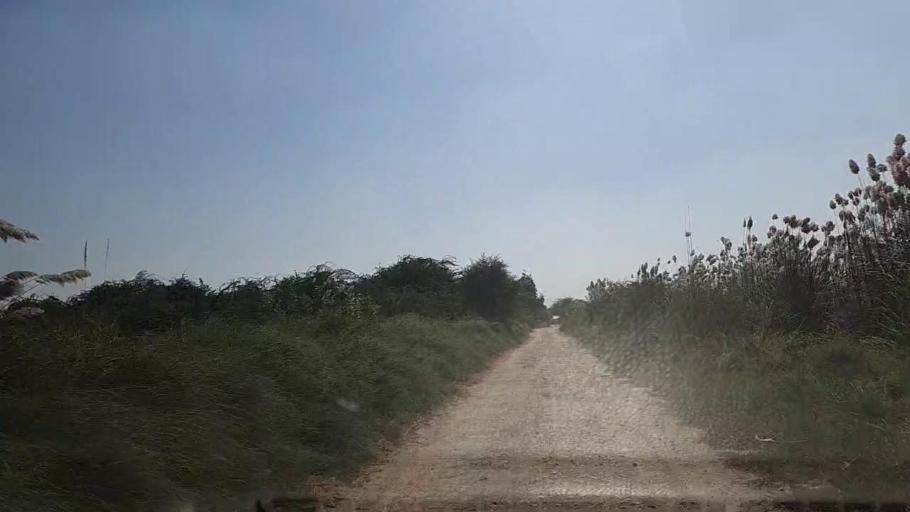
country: PK
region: Sindh
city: Daro Mehar
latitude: 24.8218
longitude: 68.0857
